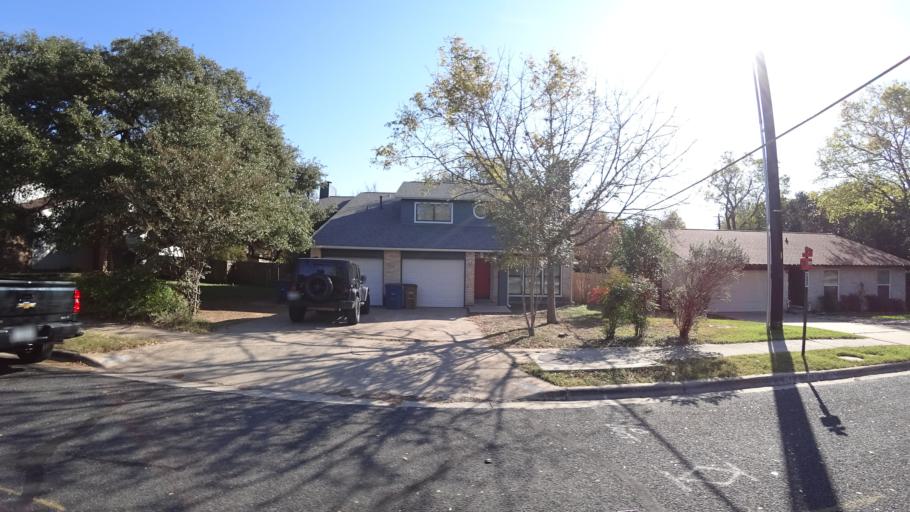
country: US
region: Texas
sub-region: Travis County
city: Barton Creek
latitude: 30.2300
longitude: -97.8461
